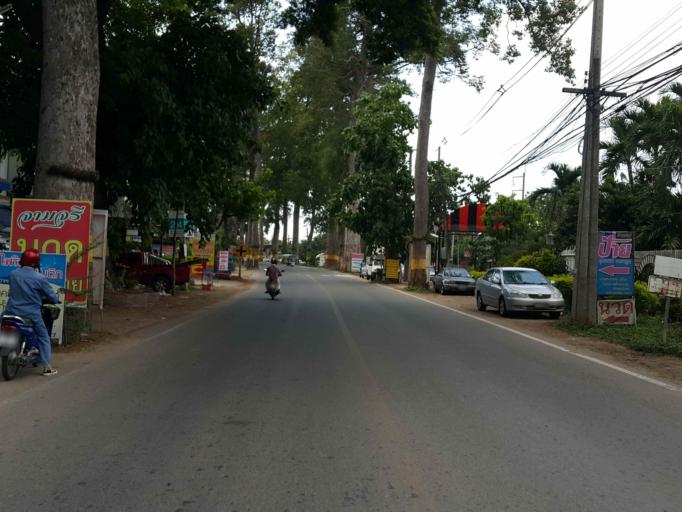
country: TH
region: Chiang Mai
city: Saraphi
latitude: 18.7276
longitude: 99.0240
